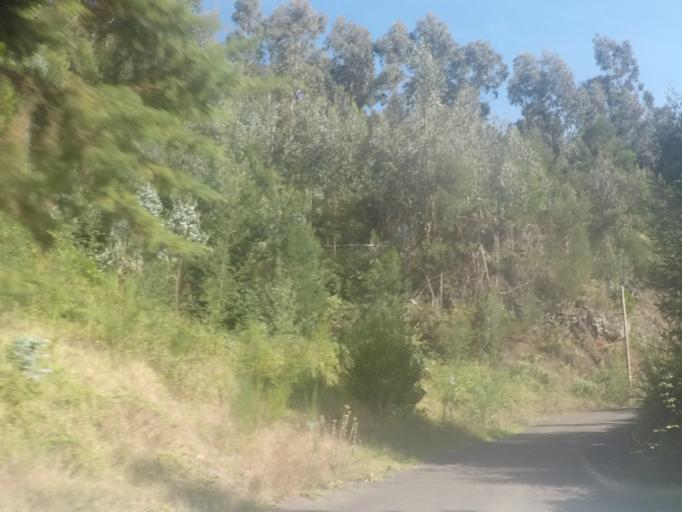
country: PT
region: Madeira
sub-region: Funchal
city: Nossa Senhora do Monte
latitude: 32.6950
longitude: -16.9075
